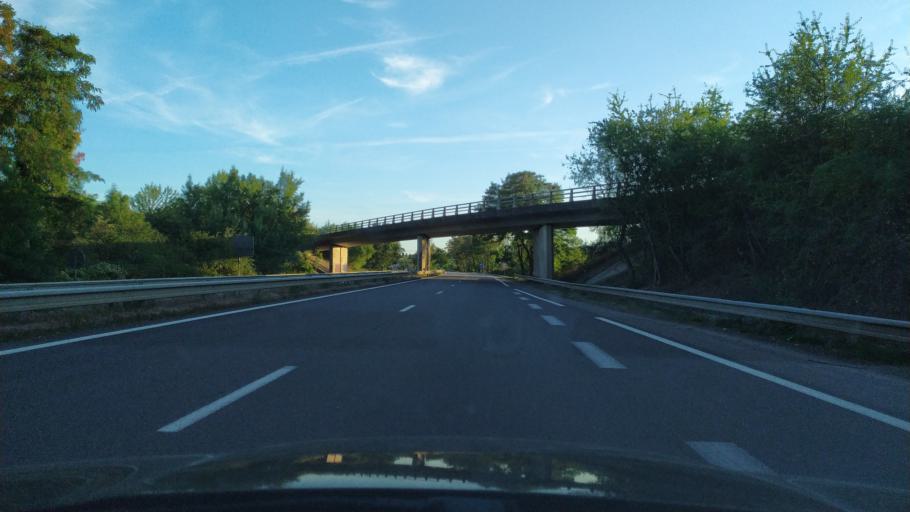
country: FR
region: Lorraine
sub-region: Departement de la Moselle
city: Maizieres-les-Metz
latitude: 49.2076
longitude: 6.1491
